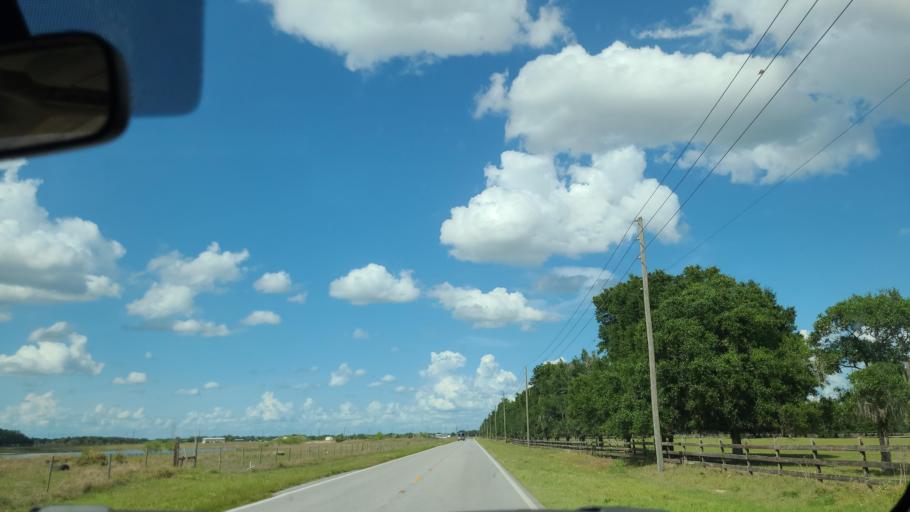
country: US
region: Florida
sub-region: Polk County
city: Lake Wales
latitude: 27.9186
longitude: -81.5458
